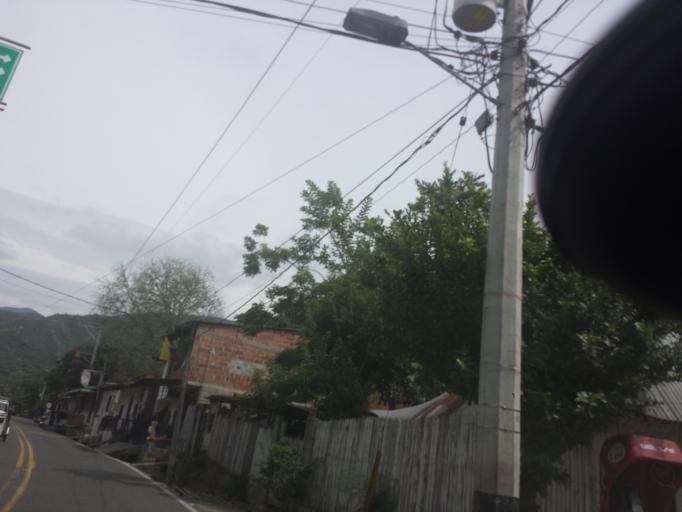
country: CO
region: Antioquia
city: Antioquia
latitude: 6.5620
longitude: -75.8307
